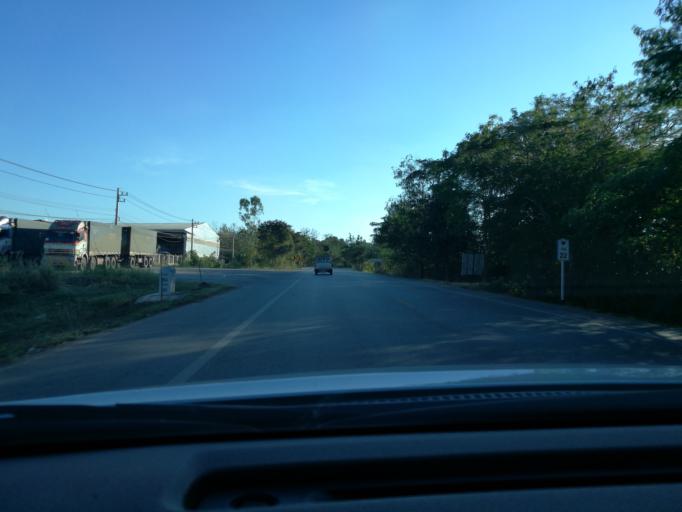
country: TH
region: Phitsanulok
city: Nakhon Thai
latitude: 17.0507
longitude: 100.8108
